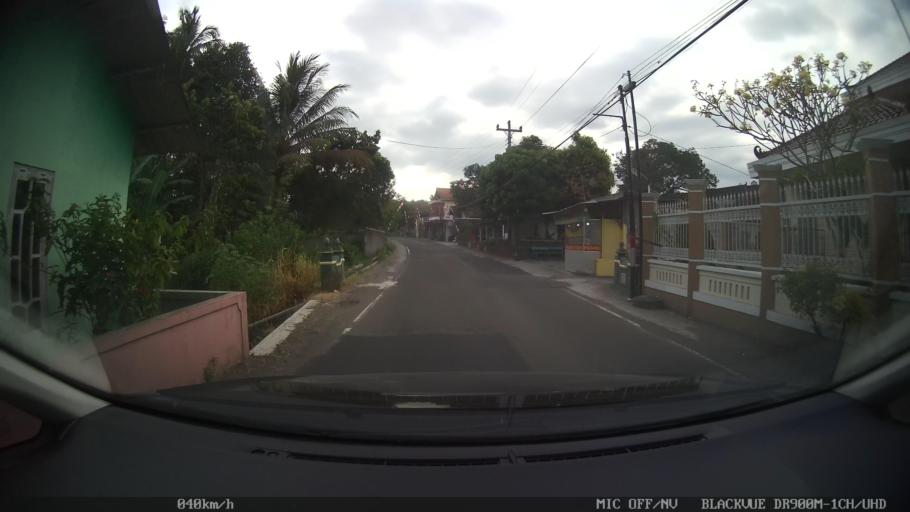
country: ID
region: Daerah Istimewa Yogyakarta
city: Depok
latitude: -7.6823
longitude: 110.4440
